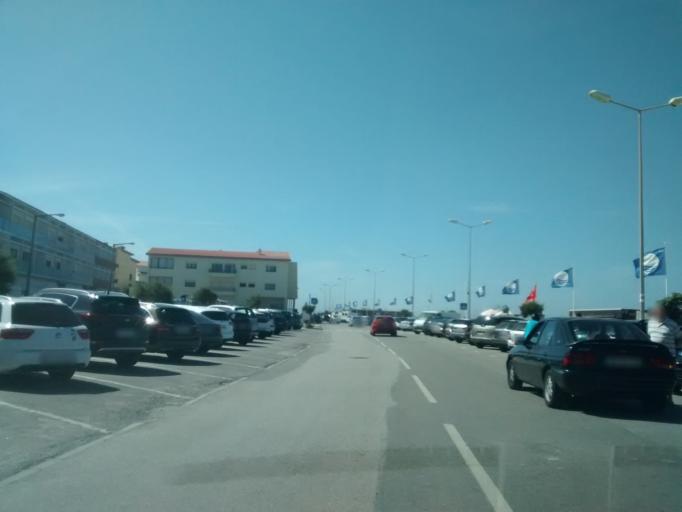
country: PT
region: Coimbra
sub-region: Mira
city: Mira
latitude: 40.4550
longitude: -8.8032
